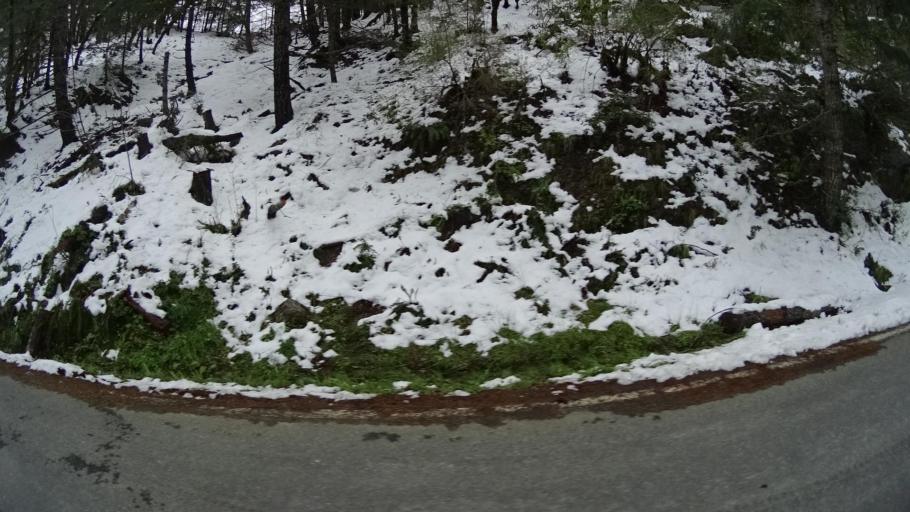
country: US
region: California
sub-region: Humboldt County
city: Willow Creek
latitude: 40.8744
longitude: -123.7563
